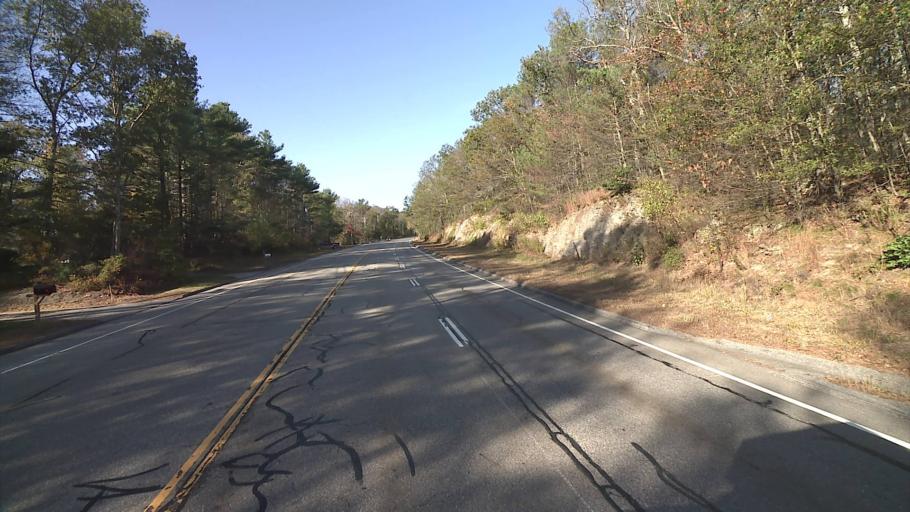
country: US
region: Rhode Island
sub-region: Providence County
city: Foster
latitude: 41.7910
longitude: -71.8041
